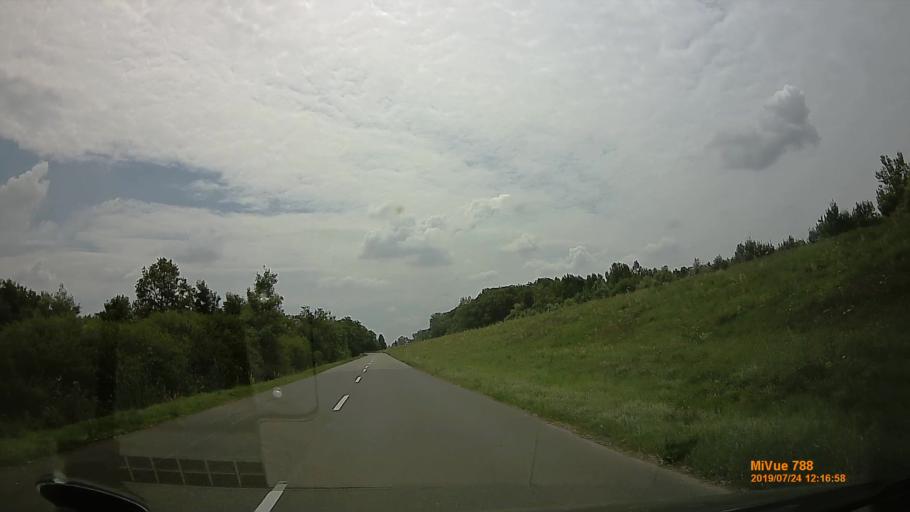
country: HU
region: Szabolcs-Szatmar-Bereg
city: Vasarosnameny
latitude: 48.1685
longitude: 22.3369
